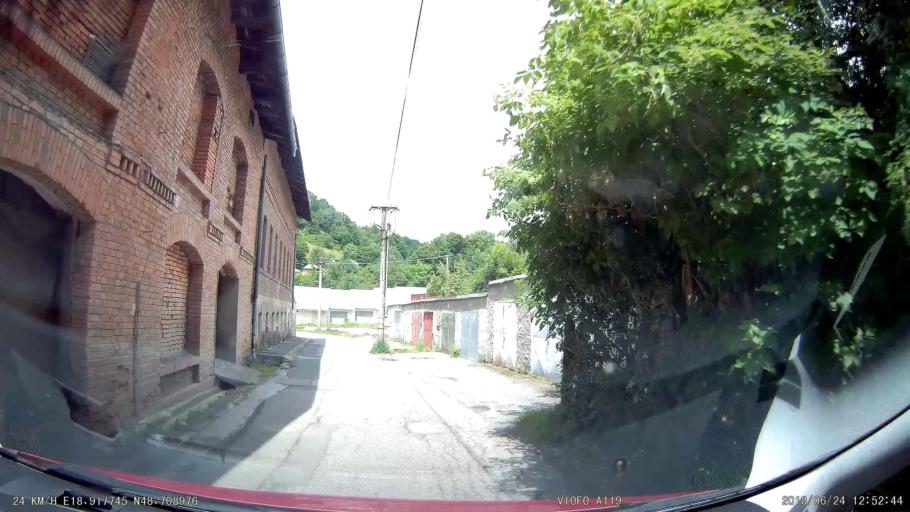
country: SK
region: Banskobystricky
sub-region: Okres Ziar nad Hronom
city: Kremnica
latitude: 48.7090
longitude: 18.9173
